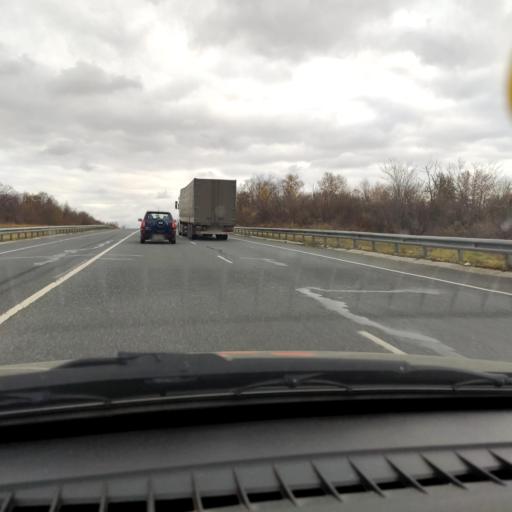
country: RU
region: Samara
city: Mezhdurechensk
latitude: 53.2568
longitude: 49.0622
